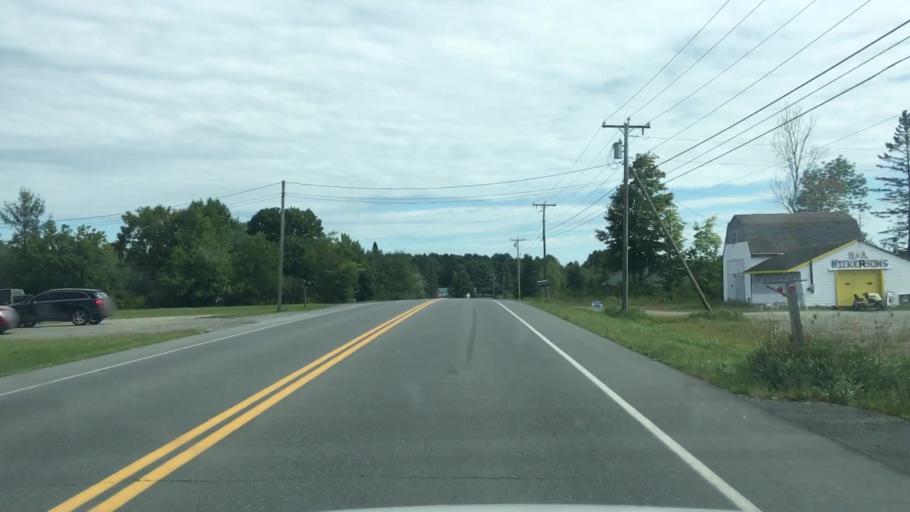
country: US
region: Maine
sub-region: Piscataquis County
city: Dover-Foxcroft
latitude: 45.1963
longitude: -69.2116
